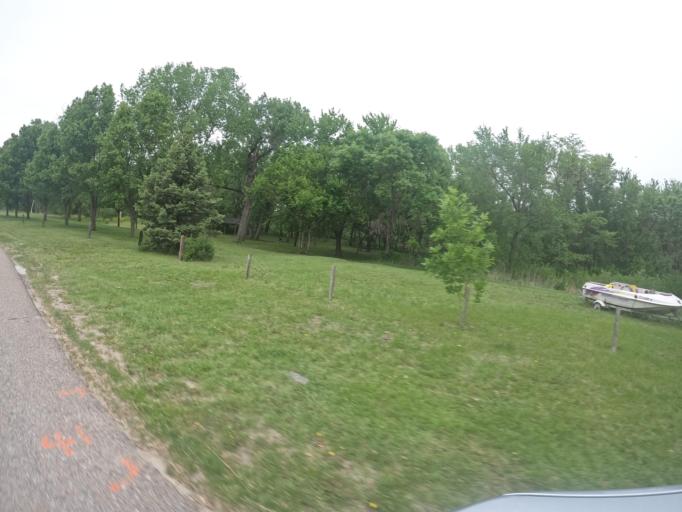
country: US
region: Nebraska
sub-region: Sarpy County
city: Offutt Air Force Base
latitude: 41.0562
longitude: -95.9532
